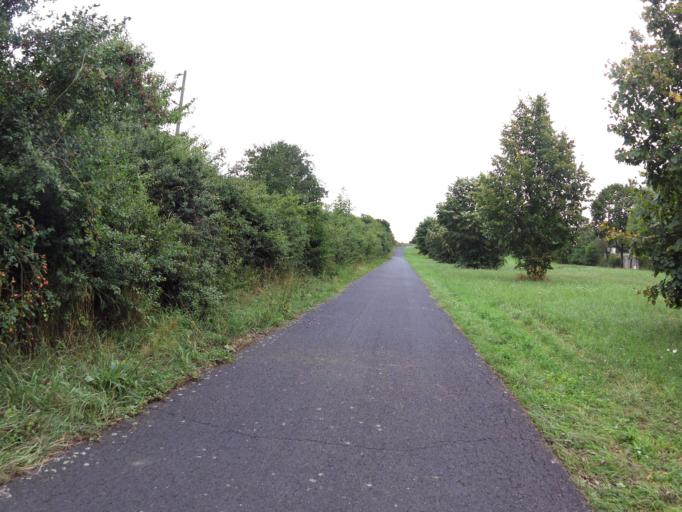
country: DE
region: Bavaria
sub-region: Regierungsbezirk Unterfranken
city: Gadheim
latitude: 50.0180
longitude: 10.3746
